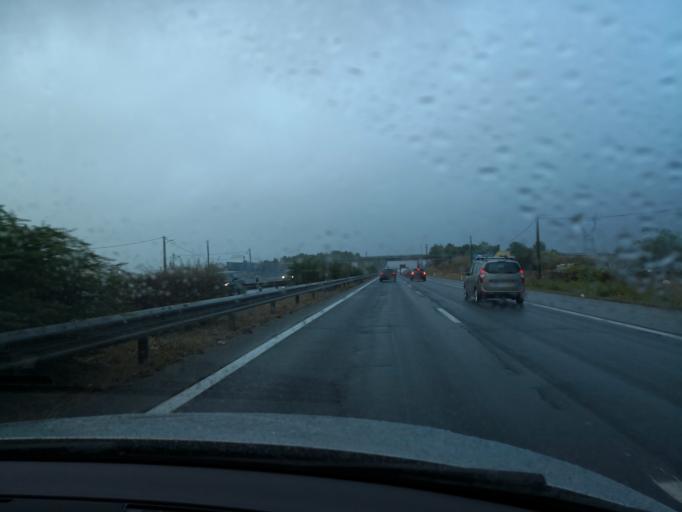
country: PT
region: Setubal
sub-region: Moita
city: Moita
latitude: 38.6578
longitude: -8.9628
